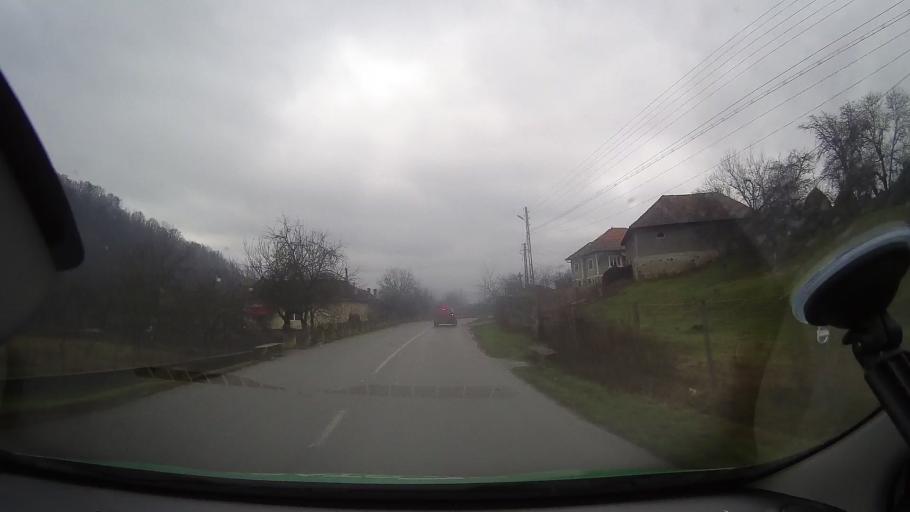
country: RO
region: Hunedoara
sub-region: Comuna Tomesti
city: Tomesti
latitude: 46.1982
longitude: 22.6474
